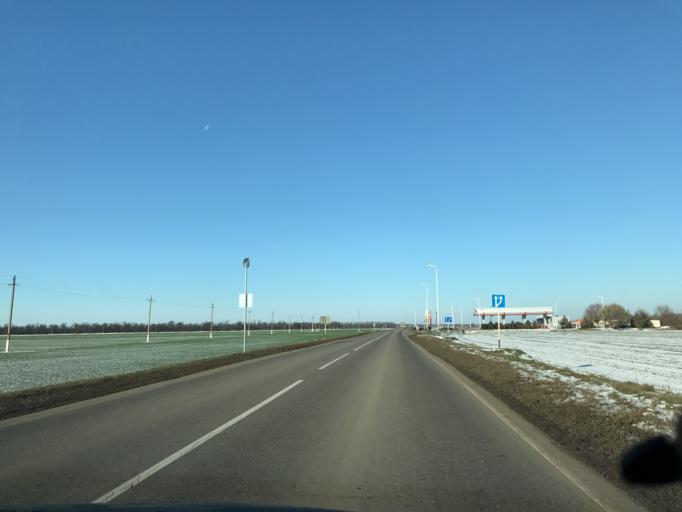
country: RU
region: Rostov
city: Peschanokopskoye
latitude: 46.2731
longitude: 40.9659
